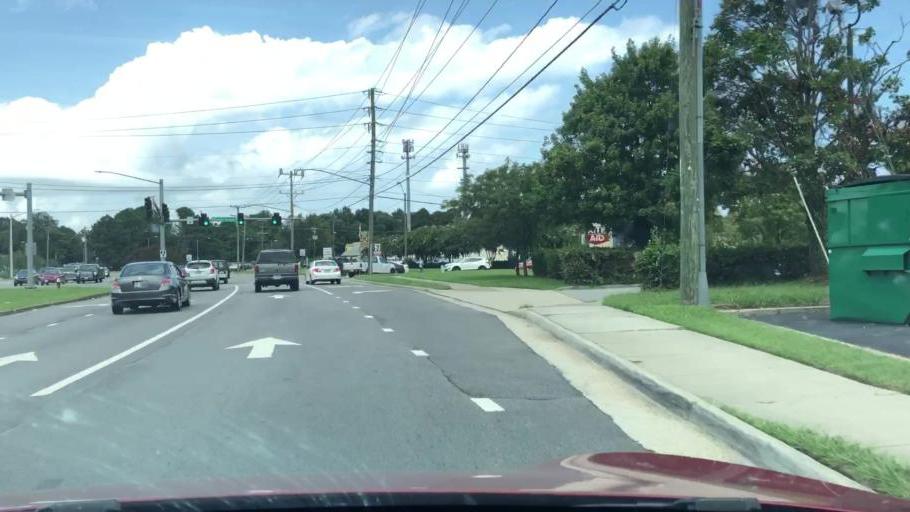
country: US
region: Virginia
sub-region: City of Norfolk
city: Norfolk
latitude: 36.8938
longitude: -76.1410
